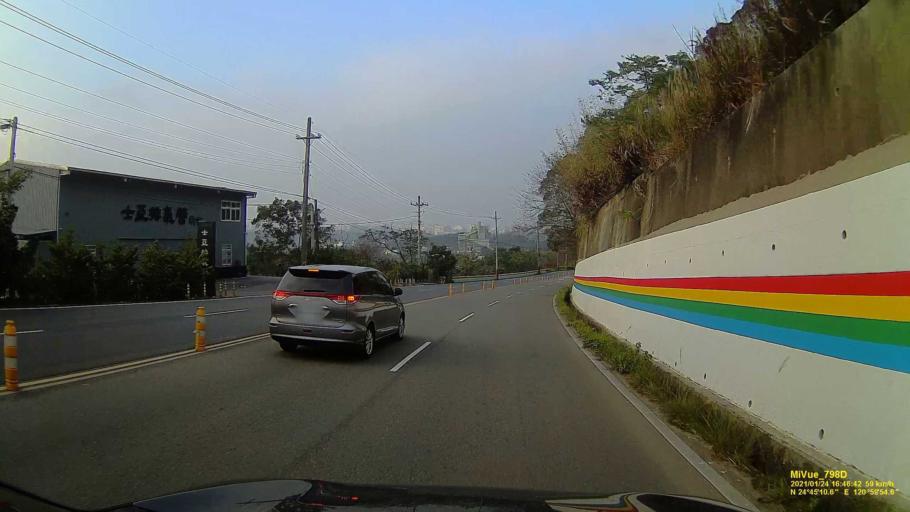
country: TW
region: Taiwan
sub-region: Hsinchu
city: Hsinchu
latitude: 24.7533
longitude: 120.9985
